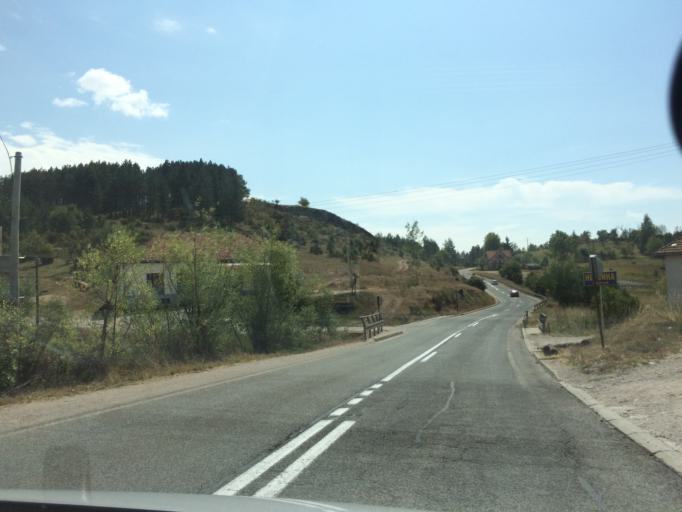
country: RS
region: Central Serbia
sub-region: Zlatiborski Okrug
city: Nova Varos
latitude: 43.5443
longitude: 19.7869
